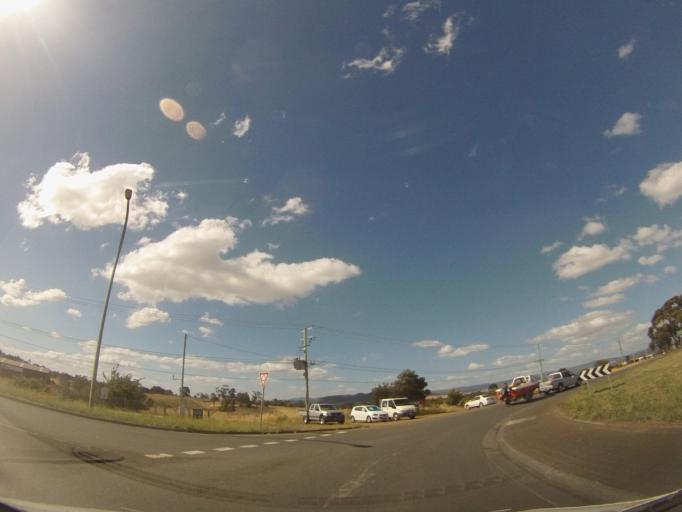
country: AU
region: Tasmania
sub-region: Clarence
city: Cambridge
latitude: -42.8340
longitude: 147.4549
